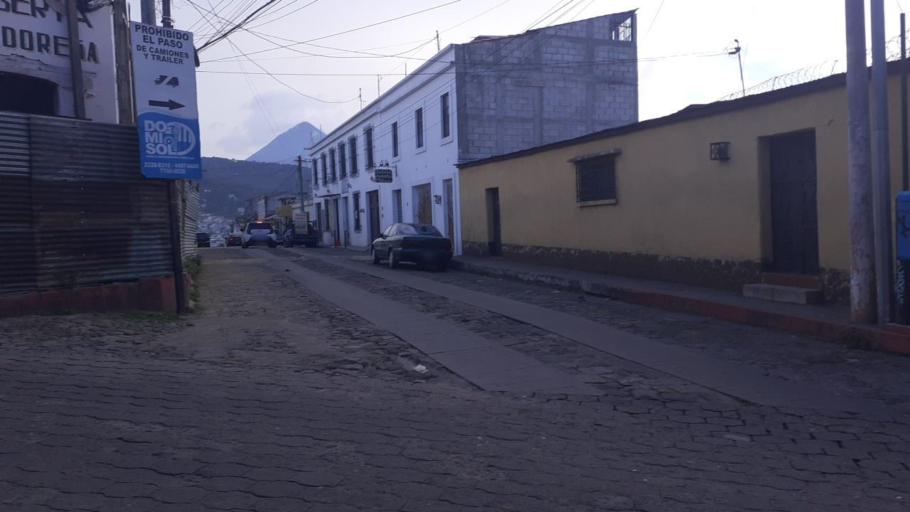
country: GT
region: Quetzaltenango
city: Quetzaltenango
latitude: 14.8402
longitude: -91.5236
